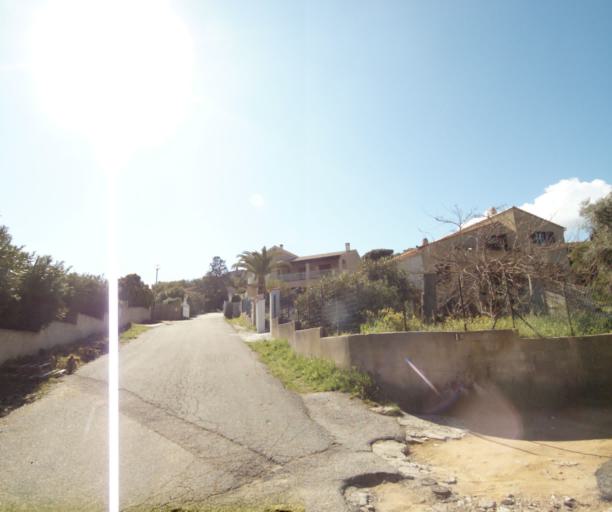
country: FR
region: Corsica
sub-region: Departement de la Corse-du-Sud
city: Propriano
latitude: 41.6709
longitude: 8.9101
